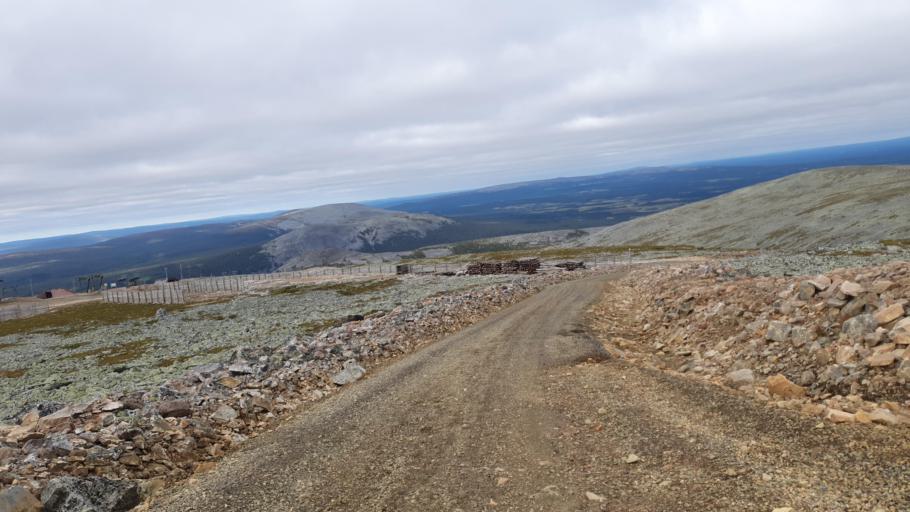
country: FI
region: Lapland
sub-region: Tunturi-Lappi
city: Kolari
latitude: 67.5686
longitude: 24.2101
